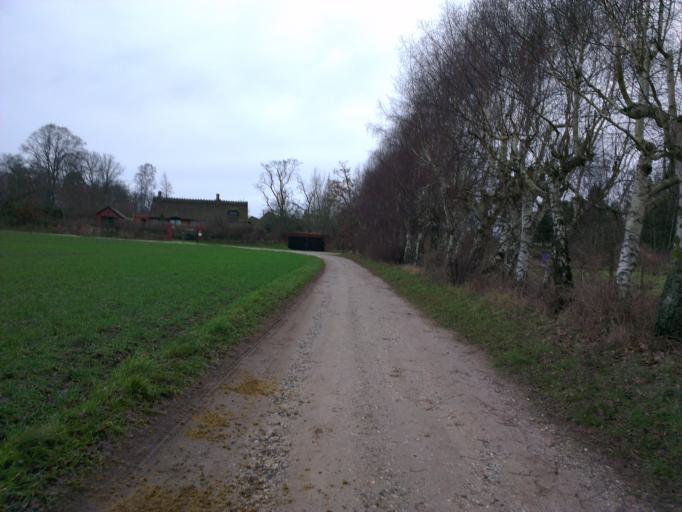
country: DK
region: Capital Region
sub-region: Frederikssund Kommune
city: Jaegerspris
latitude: 55.8485
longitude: 12.0092
